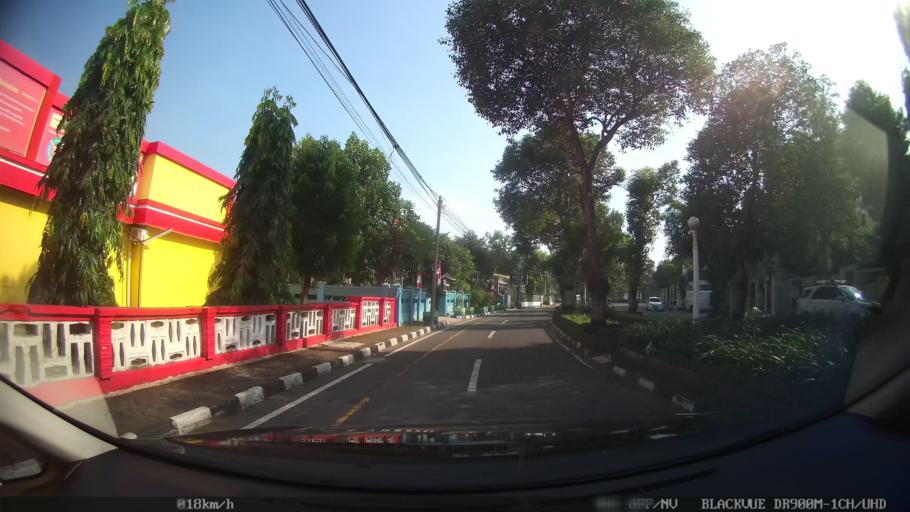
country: ID
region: Daerah Istimewa Yogyakarta
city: Yogyakarta
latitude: -7.7877
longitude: 110.3721
